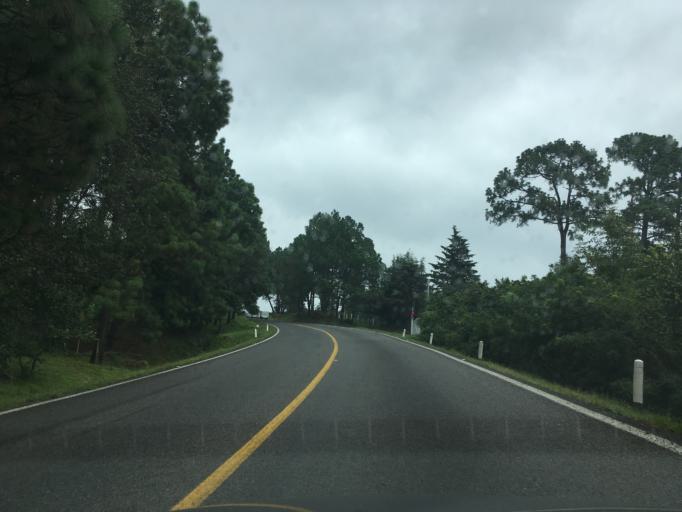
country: MX
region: Michoacan
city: Tingambato
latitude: 19.4832
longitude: -101.8881
